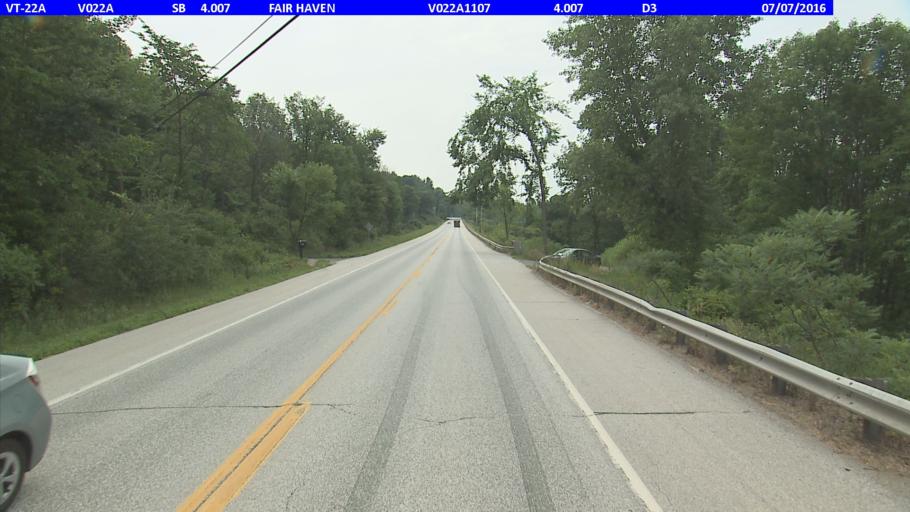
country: US
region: Vermont
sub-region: Rutland County
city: Fair Haven
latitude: 43.6221
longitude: -73.2978
